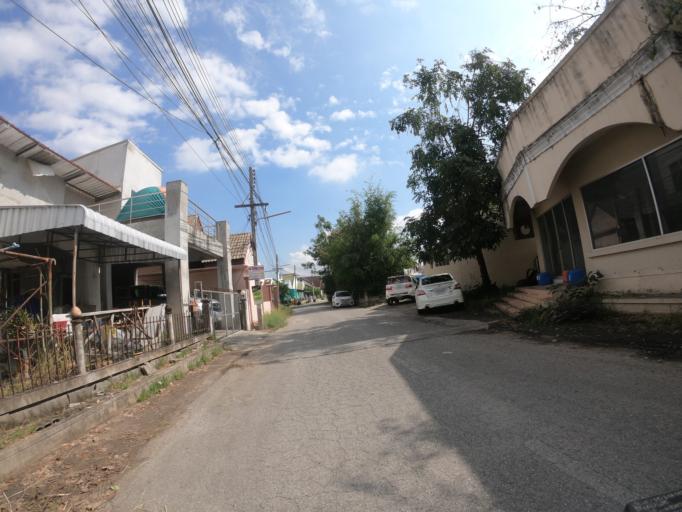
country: TH
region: Chiang Mai
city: Chiang Mai
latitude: 18.7353
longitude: 98.9589
